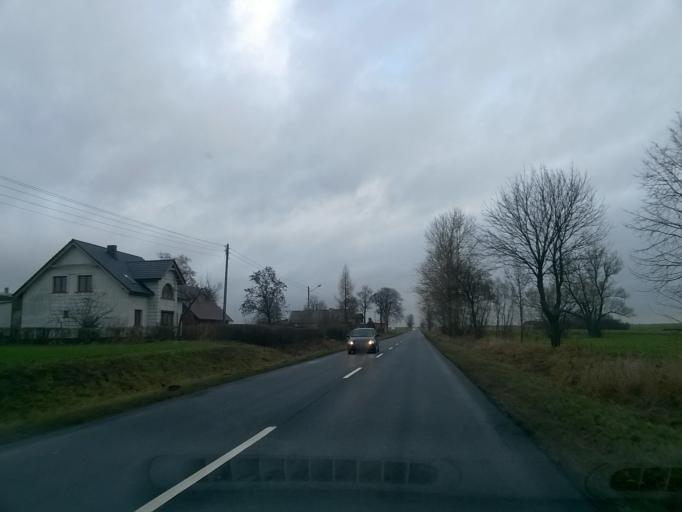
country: PL
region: Greater Poland Voivodeship
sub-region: Powiat wagrowiecki
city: Golancz
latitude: 52.9172
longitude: 17.3703
